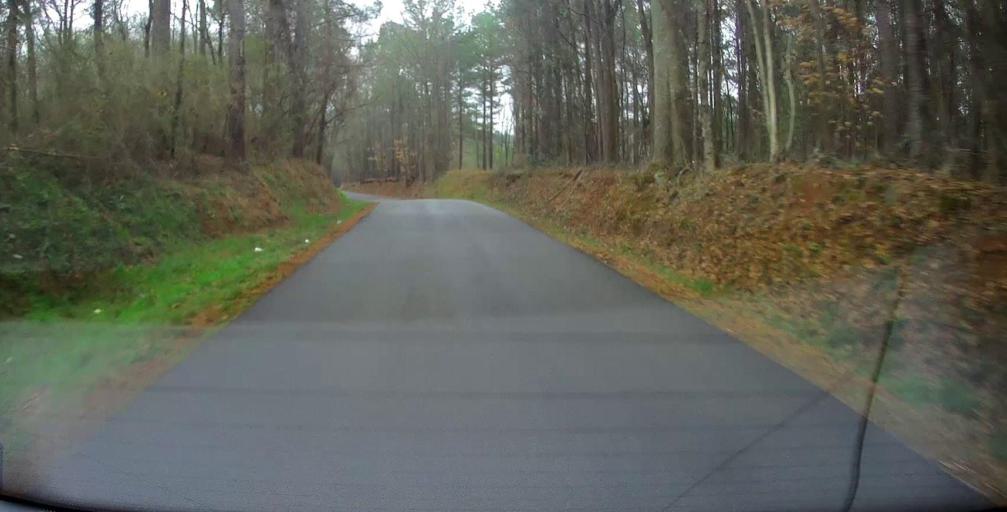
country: US
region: Georgia
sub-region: Monroe County
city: Forsyth
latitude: 33.0516
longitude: -83.8854
